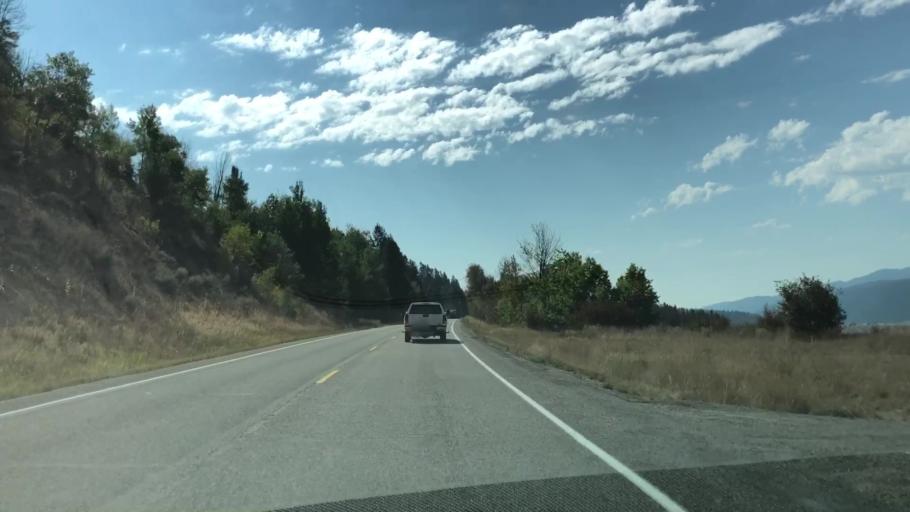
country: US
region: Idaho
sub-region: Teton County
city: Victor
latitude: 43.2927
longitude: -111.1248
